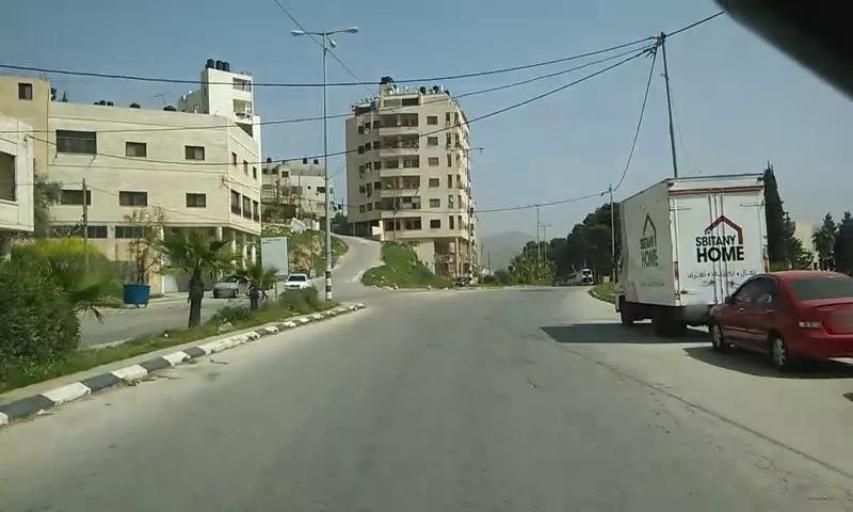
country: PS
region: West Bank
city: Balatah
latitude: 32.2170
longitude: 35.2916
